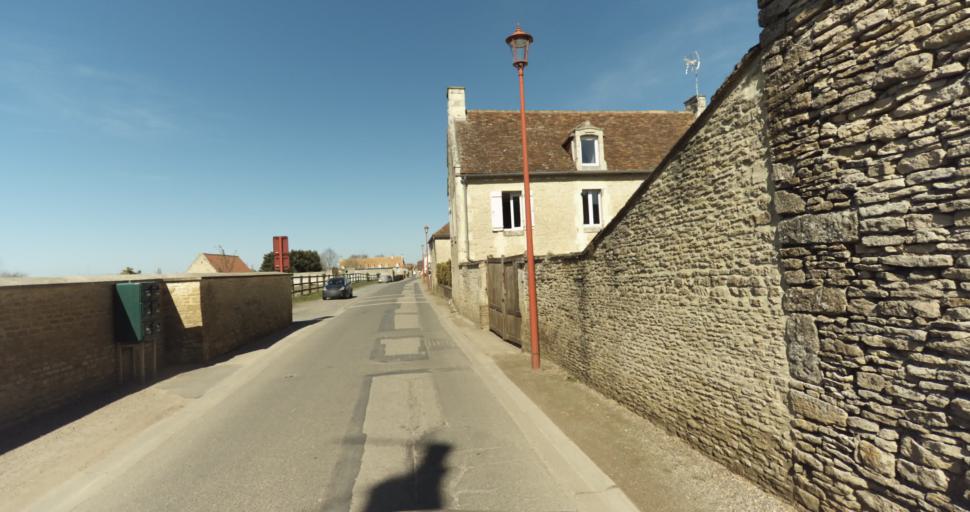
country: FR
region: Lower Normandy
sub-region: Departement du Calvados
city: Canon
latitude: 49.0519
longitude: -0.0643
